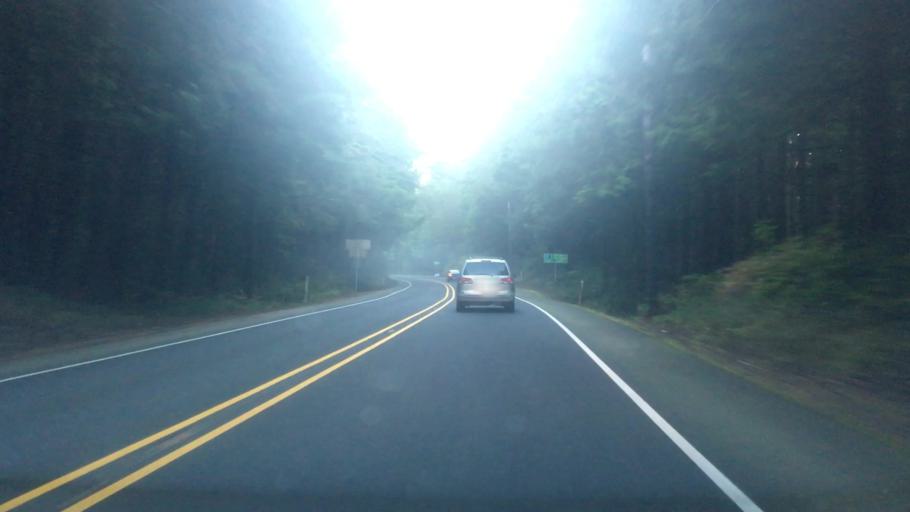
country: US
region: Oregon
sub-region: Clatsop County
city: Cannon Beach
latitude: 45.7835
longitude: -123.9576
